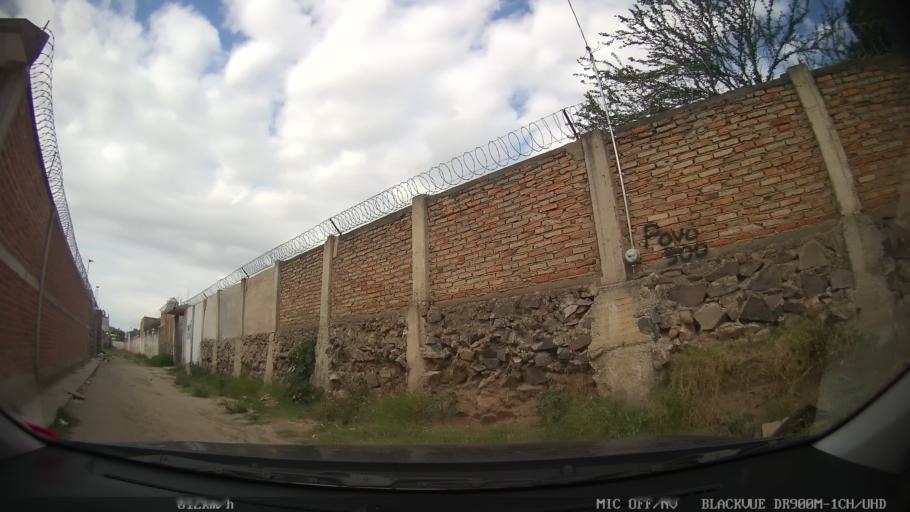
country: MX
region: Jalisco
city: Tonala
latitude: 20.6660
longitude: -103.2411
